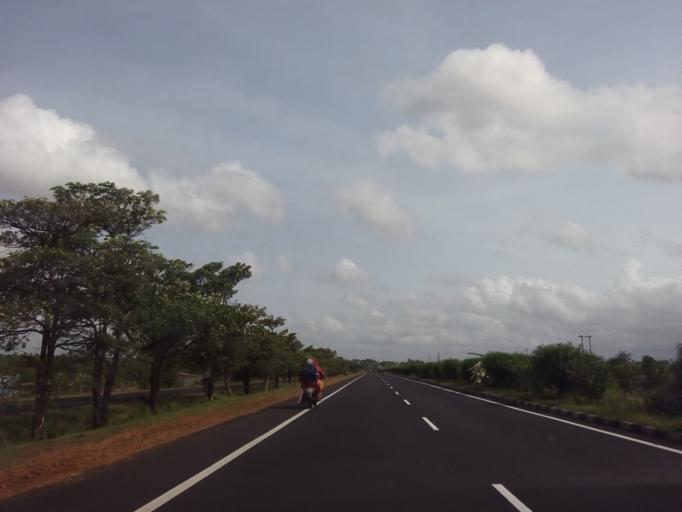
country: IN
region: Karnataka
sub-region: Belgaum
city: Sankeshwar
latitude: 16.1632
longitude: 74.5184
